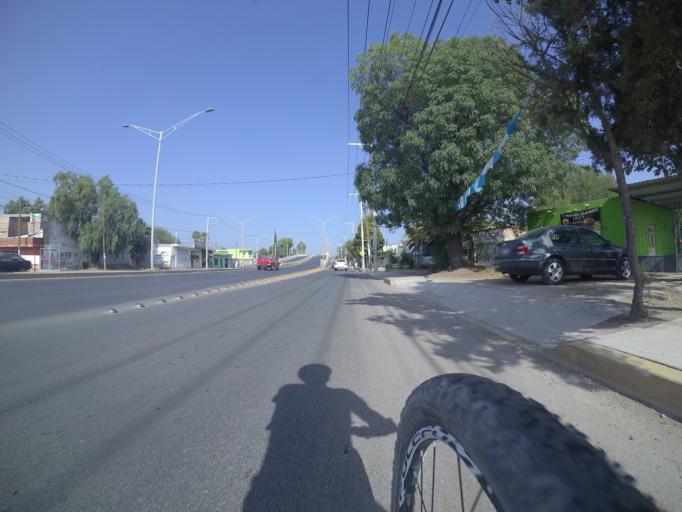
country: MX
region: Aguascalientes
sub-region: Jesus Maria
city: Corral de Barrancos
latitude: 21.9523
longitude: -102.3324
